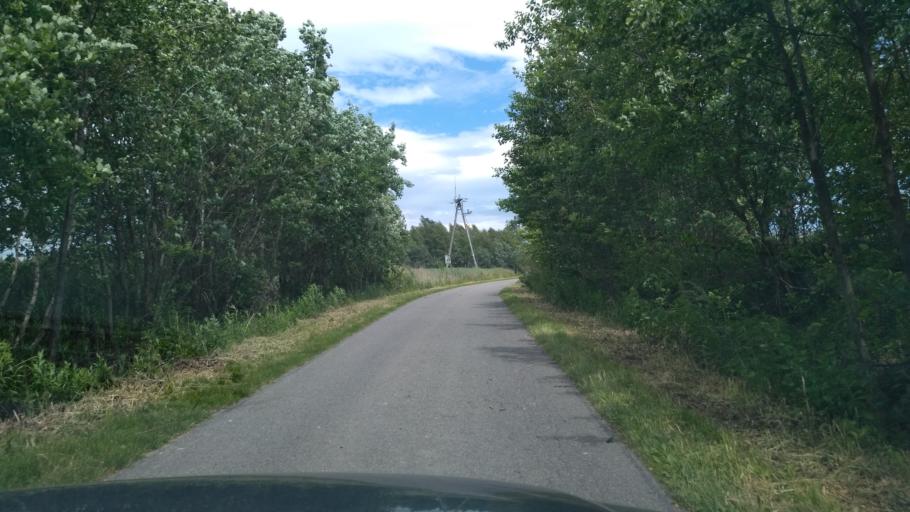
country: PL
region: Subcarpathian Voivodeship
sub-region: Powiat ropczycko-sedziszowski
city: Wielopole Skrzynskie
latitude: 49.9732
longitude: 21.6436
